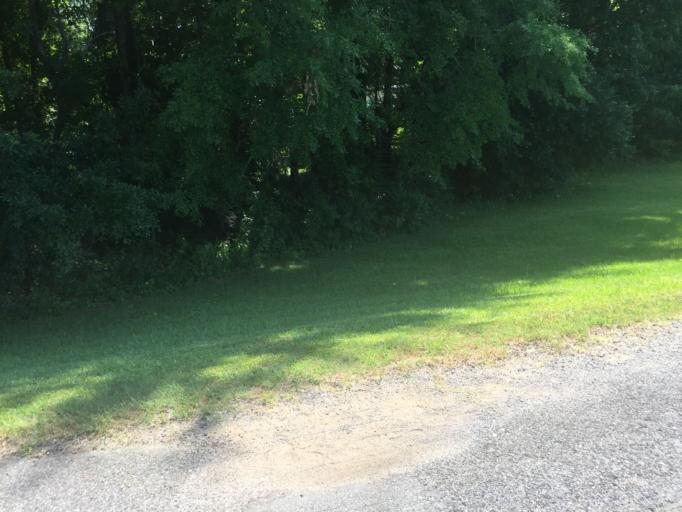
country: US
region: Alabama
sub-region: Hale County
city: Moundville
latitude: 33.0049
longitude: -87.6274
